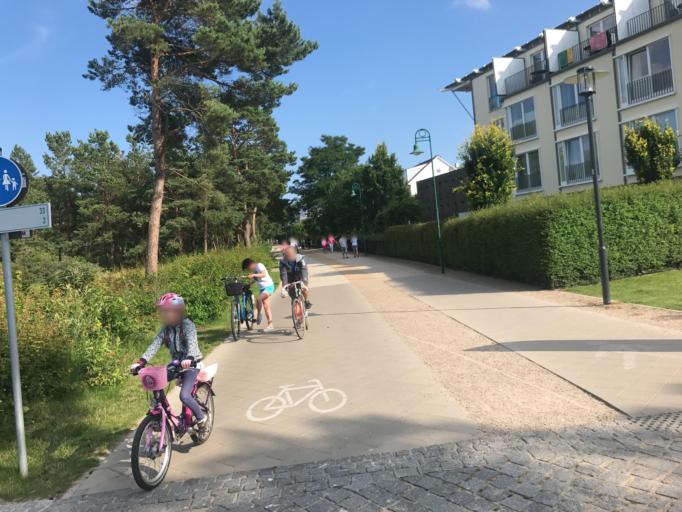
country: DE
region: Mecklenburg-Vorpommern
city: Seebad Bansin
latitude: 53.9677
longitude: 14.1513
